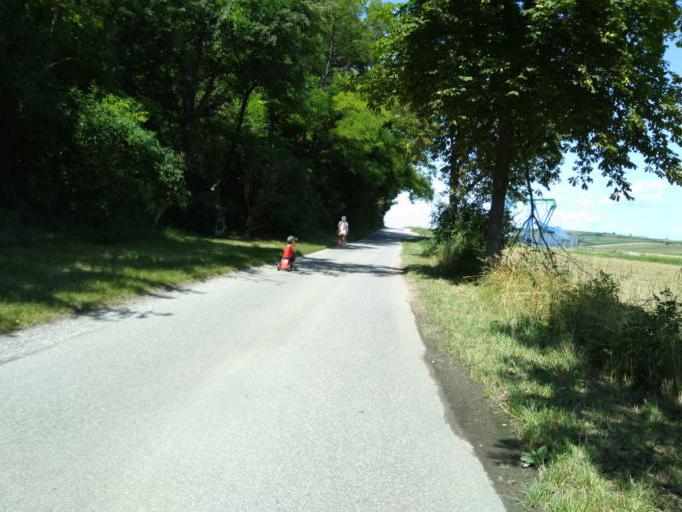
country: AT
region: Lower Austria
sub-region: Politischer Bezirk Ganserndorf
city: Auersthal
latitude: 48.3744
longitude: 16.6803
